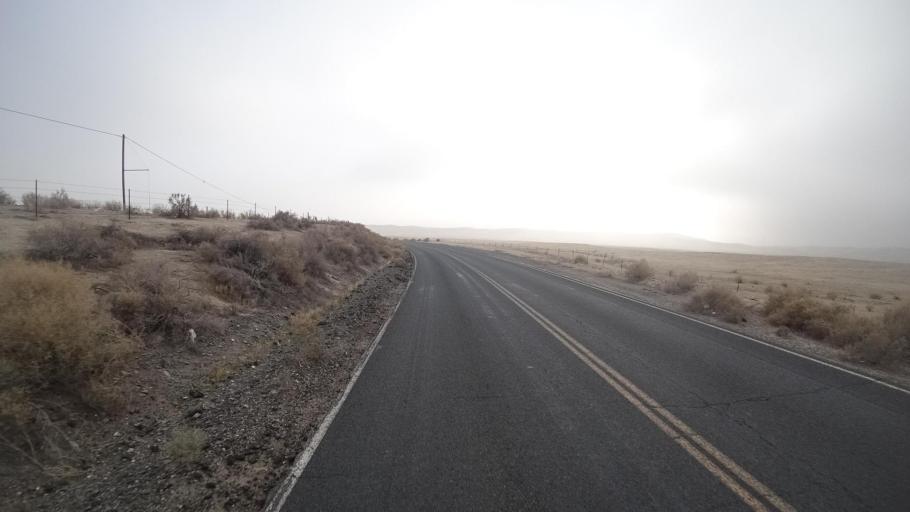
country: US
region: California
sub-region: Kern County
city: Ford City
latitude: 35.2532
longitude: -119.4644
